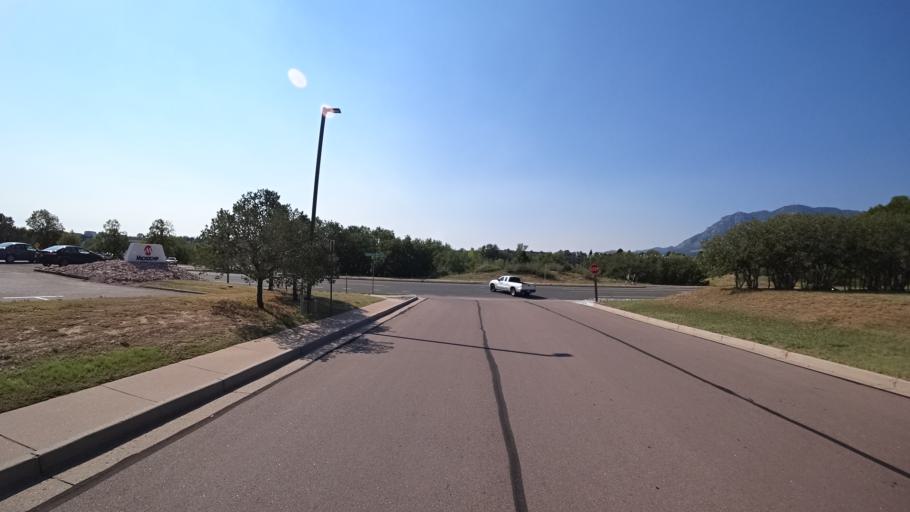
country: US
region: Colorado
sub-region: El Paso County
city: Stratmoor
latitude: 38.7873
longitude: -104.8071
